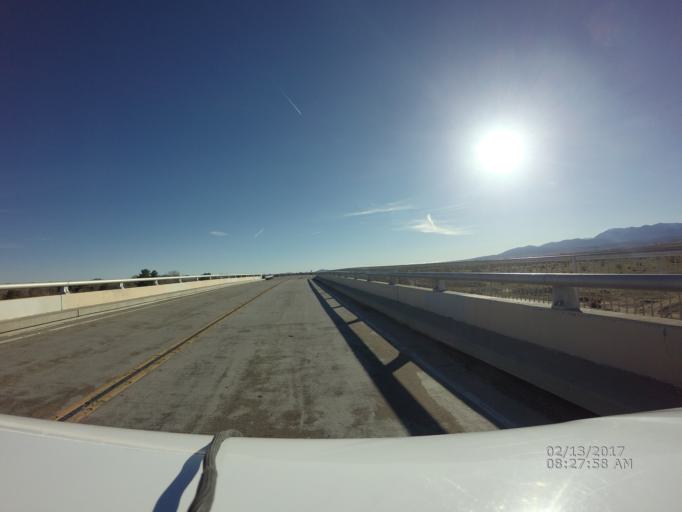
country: US
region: California
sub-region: Los Angeles County
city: Littlerock
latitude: 34.5434
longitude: -117.9542
